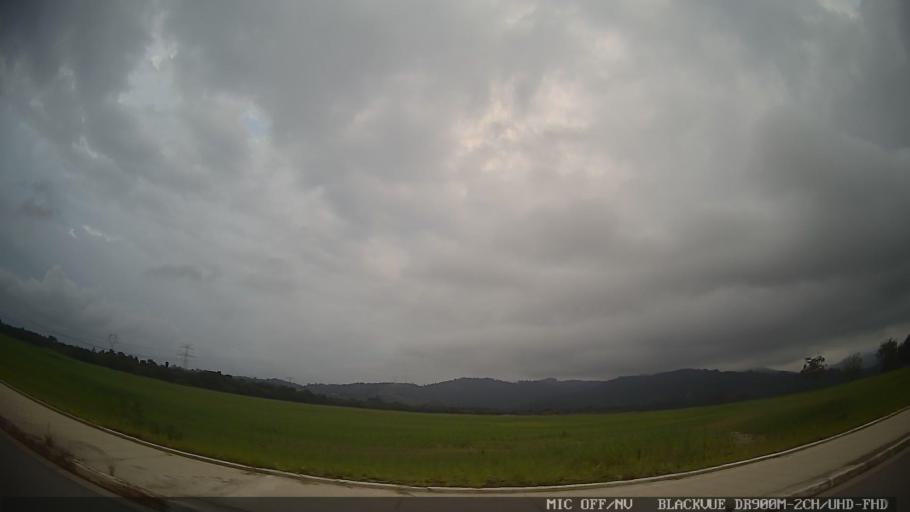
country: BR
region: Sao Paulo
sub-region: Mogi das Cruzes
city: Mogi das Cruzes
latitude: -23.5404
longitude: -46.2427
